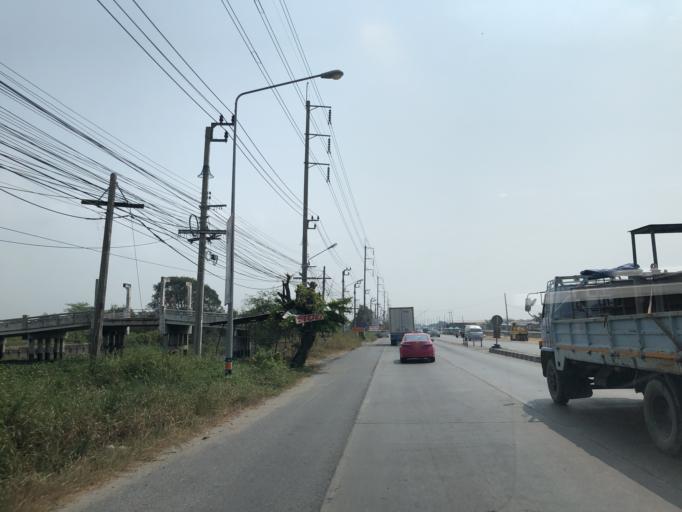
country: TH
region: Samut Prakan
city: Bang Bo District
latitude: 13.5127
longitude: 100.7905
